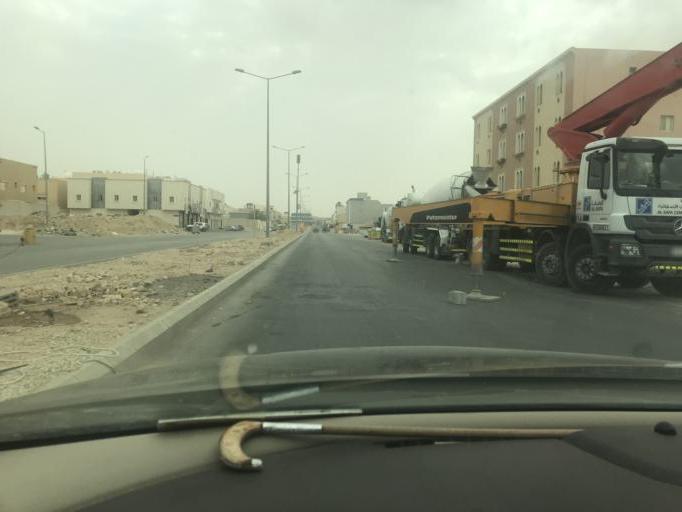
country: SA
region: Ar Riyad
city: Riyadh
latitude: 24.8125
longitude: 46.6067
